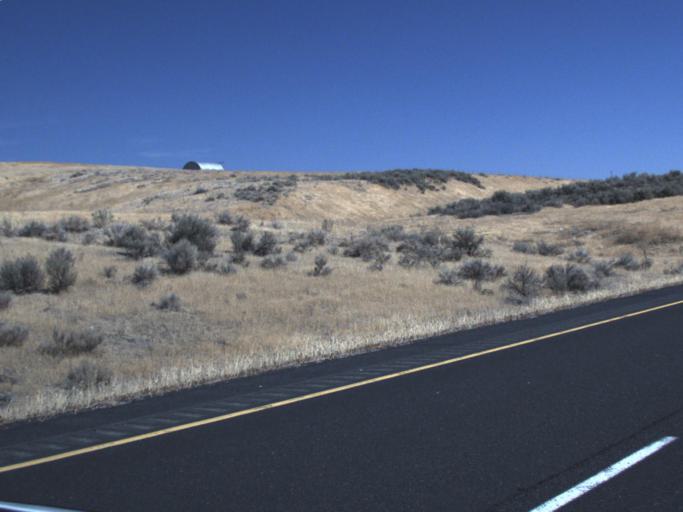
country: US
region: Washington
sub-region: Grant County
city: Warden
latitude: 47.0843
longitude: -118.9649
